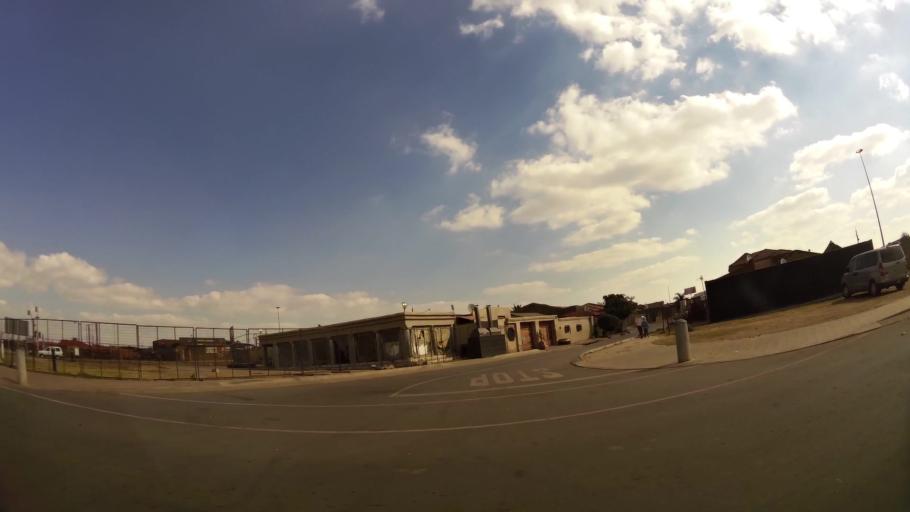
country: ZA
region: Gauteng
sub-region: Ekurhuleni Metropolitan Municipality
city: Tembisa
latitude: -25.9967
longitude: 28.2362
